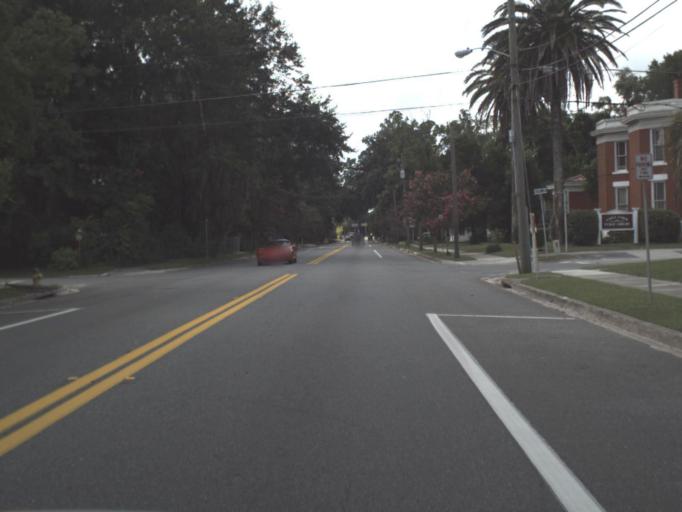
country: US
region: Florida
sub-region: Baker County
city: Macclenny
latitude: 30.2809
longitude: -82.1220
